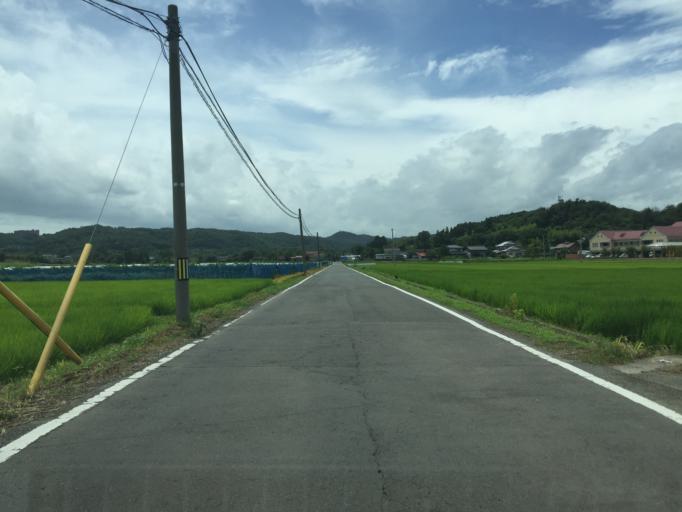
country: JP
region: Fukushima
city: Fukushima-shi
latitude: 37.7159
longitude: 140.4486
